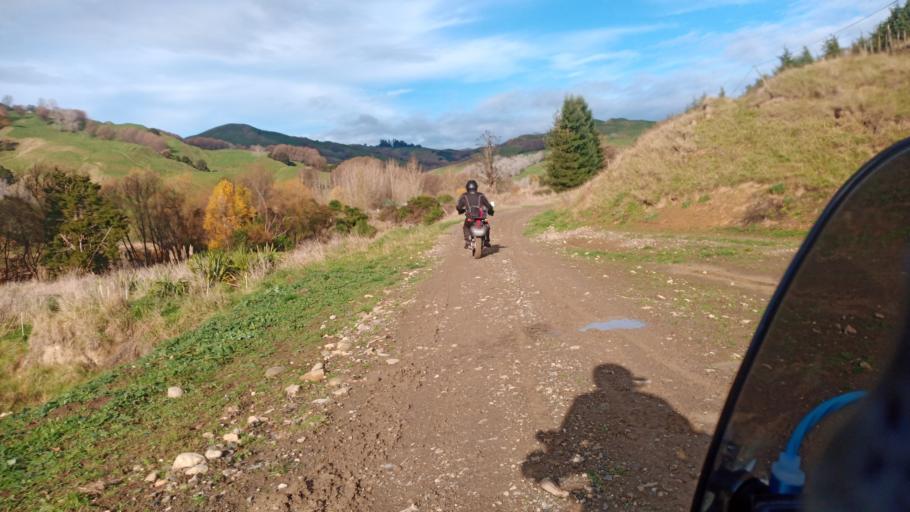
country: NZ
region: Gisborne
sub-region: Gisborne District
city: Gisborne
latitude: -38.3469
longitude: 177.9372
